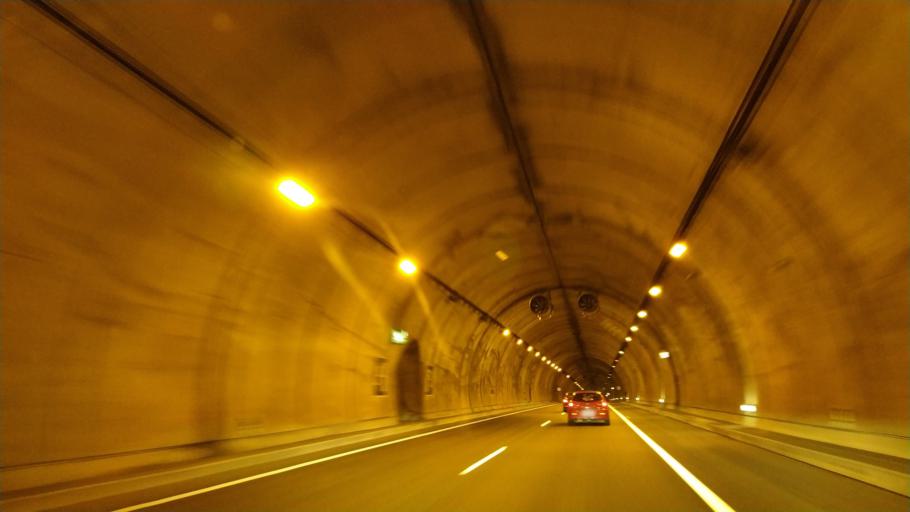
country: ES
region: Cantabria
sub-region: Provincia de Cantabria
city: Arenas de Iguna
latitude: 43.2055
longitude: -4.0737
